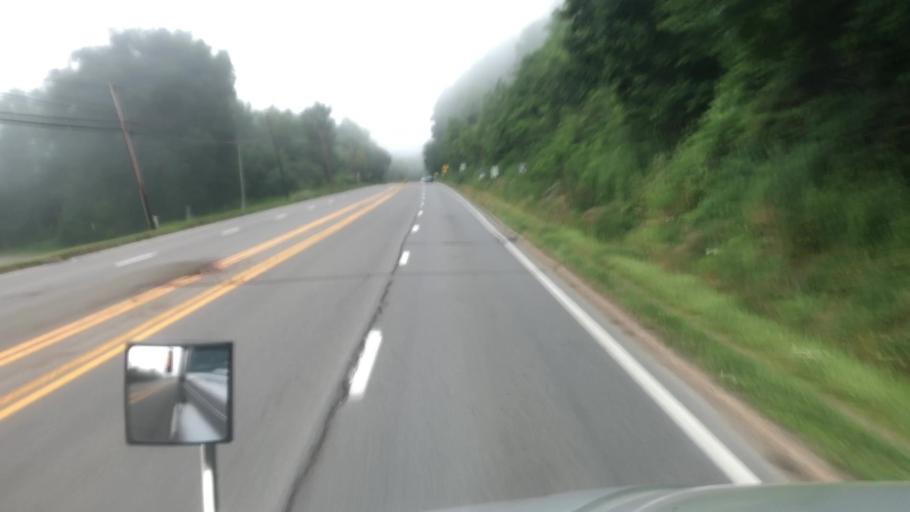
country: US
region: Pennsylvania
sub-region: Venango County
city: Franklin
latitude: 41.3980
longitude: -79.8178
